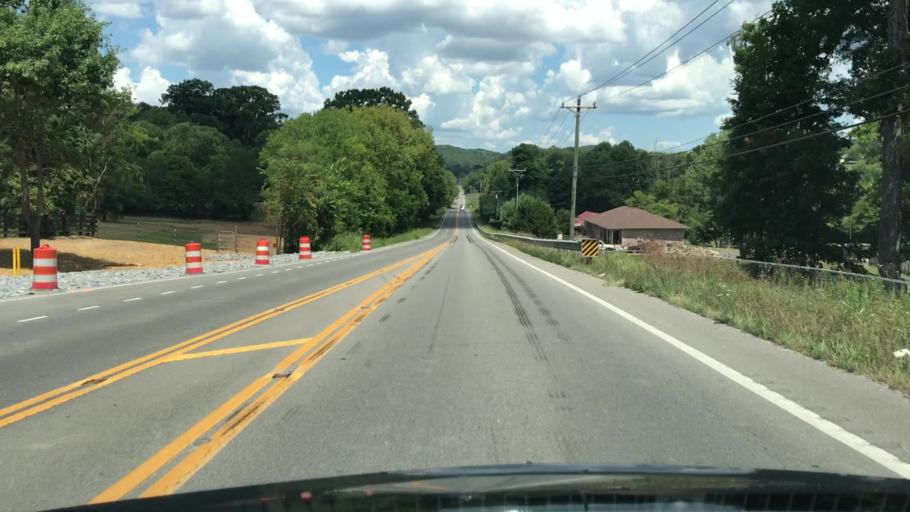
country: US
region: Tennessee
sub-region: Williamson County
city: Nolensville
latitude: 35.8794
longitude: -86.6613
